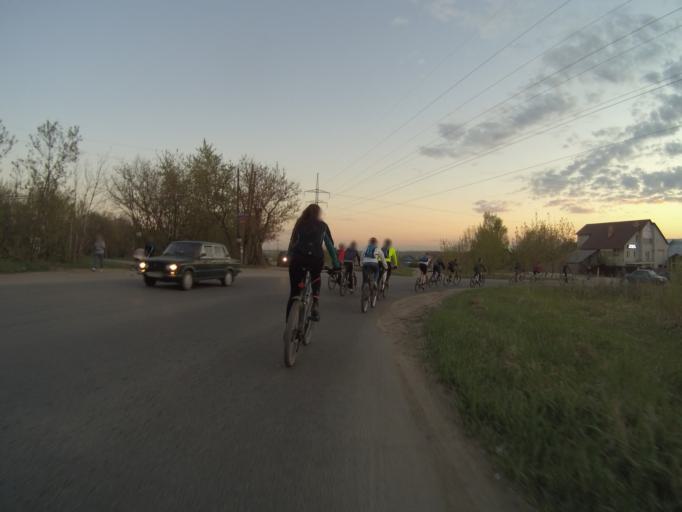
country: RU
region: Vladimir
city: Vladimir
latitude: 56.1383
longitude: 40.3527
